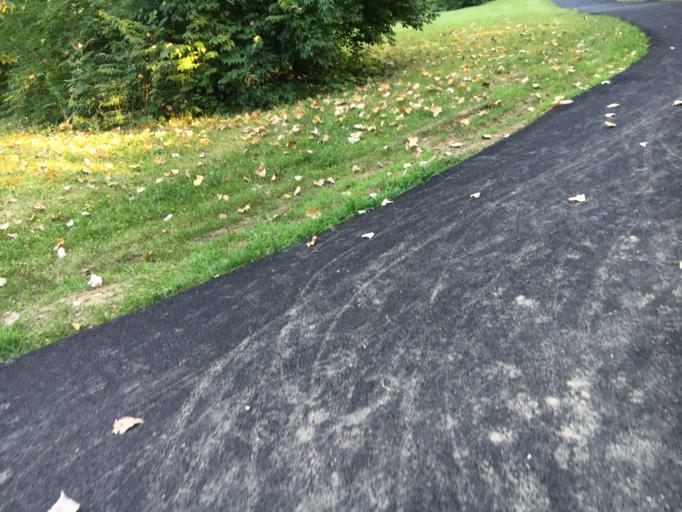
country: US
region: Ohio
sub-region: Franklin County
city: Hilliard
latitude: 39.9925
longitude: -83.1610
